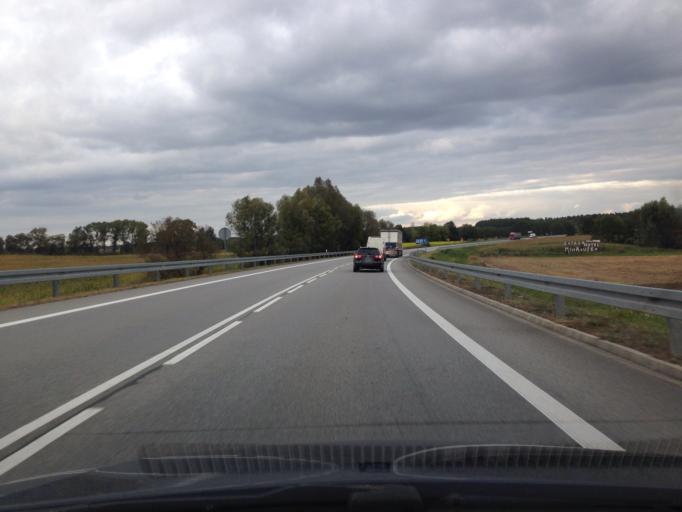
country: PL
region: Kujawsko-Pomorskie
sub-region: Powiat lipnowski
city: Skepe
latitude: 52.8735
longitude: 19.3183
